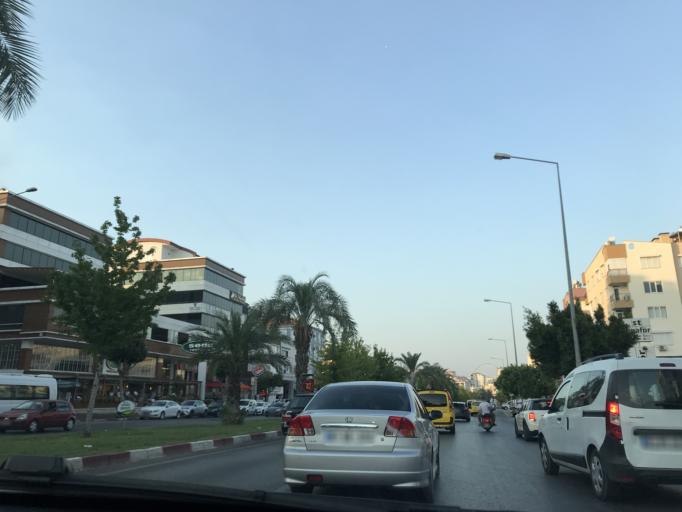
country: TR
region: Antalya
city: Antalya
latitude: 36.8758
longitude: 30.6439
